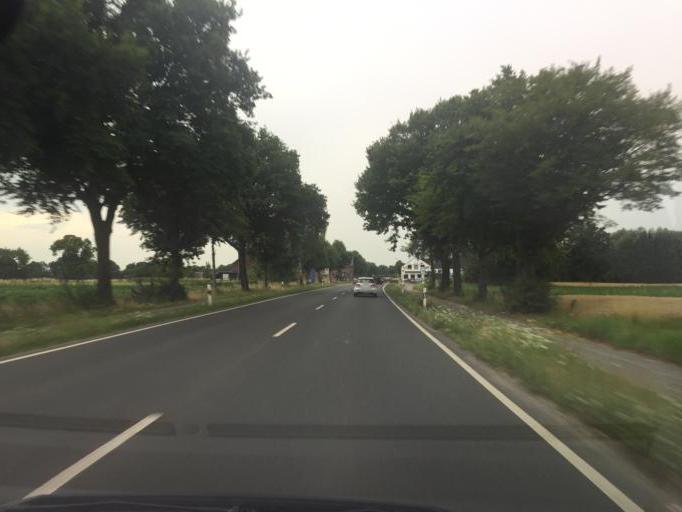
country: DE
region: North Rhine-Westphalia
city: Wegberg
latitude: 51.1375
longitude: 6.3428
